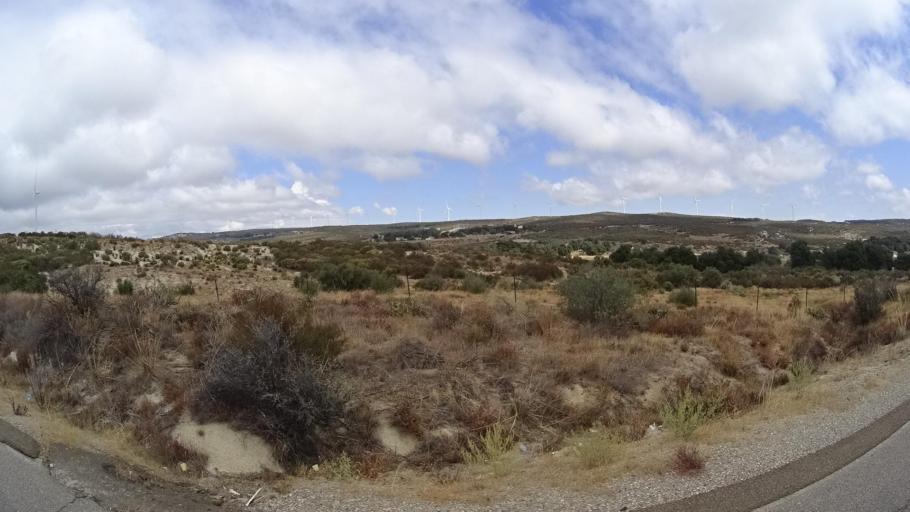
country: US
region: California
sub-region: San Diego County
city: Campo
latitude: 32.6964
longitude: -116.3477
